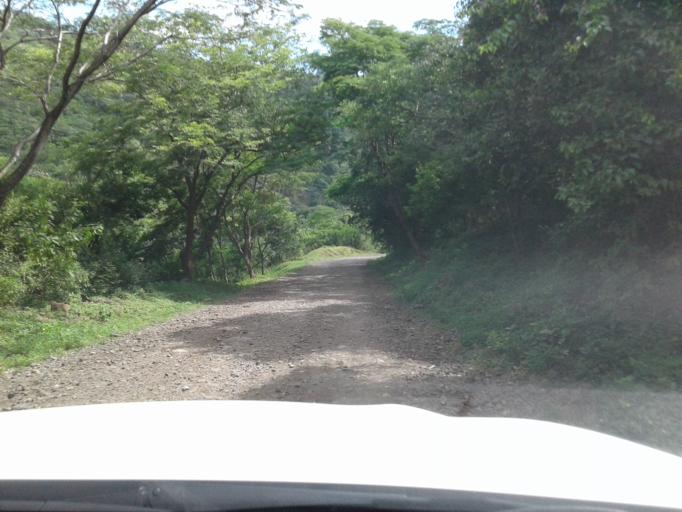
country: NI
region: Matagalpa
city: Ciudad Dario
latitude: 12.8430
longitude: -86.0547
